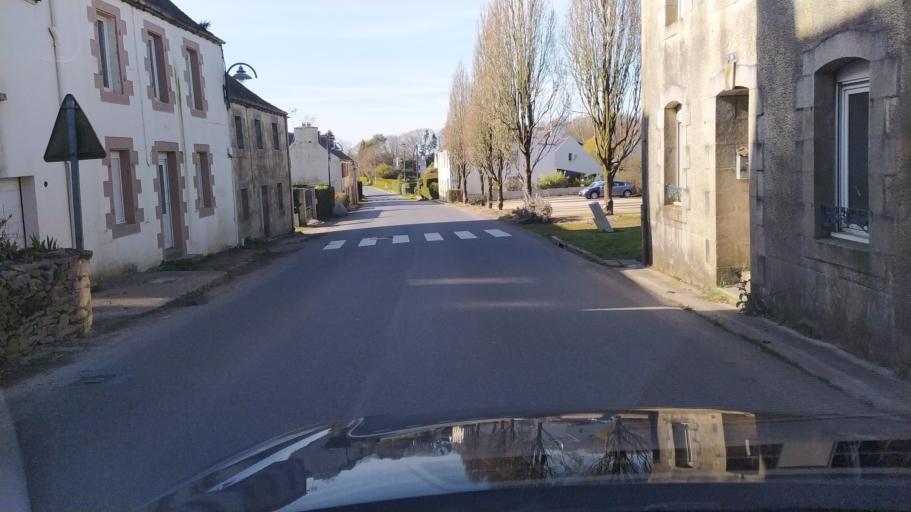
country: FR
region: Brittany
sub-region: Departement du Finistere
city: Lampaul-Guimiliau
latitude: 48.4477
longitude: -4.0062
